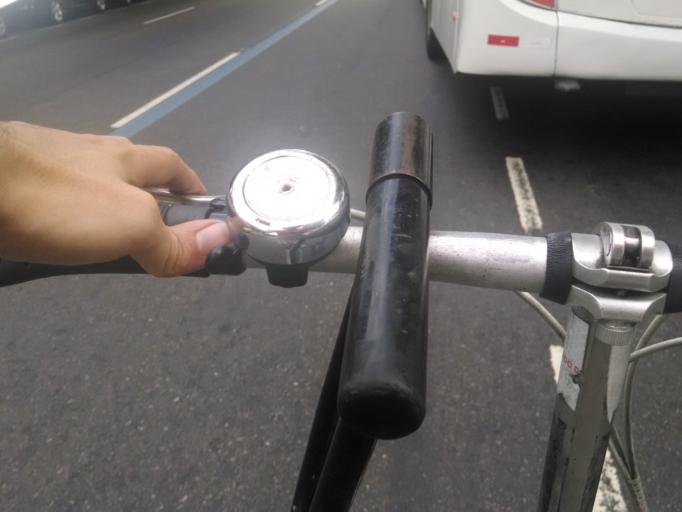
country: BR
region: Rio de Janeiro
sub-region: Rio De Janeiro
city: Rio de Janeiro
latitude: -22.9417
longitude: -43.1798
